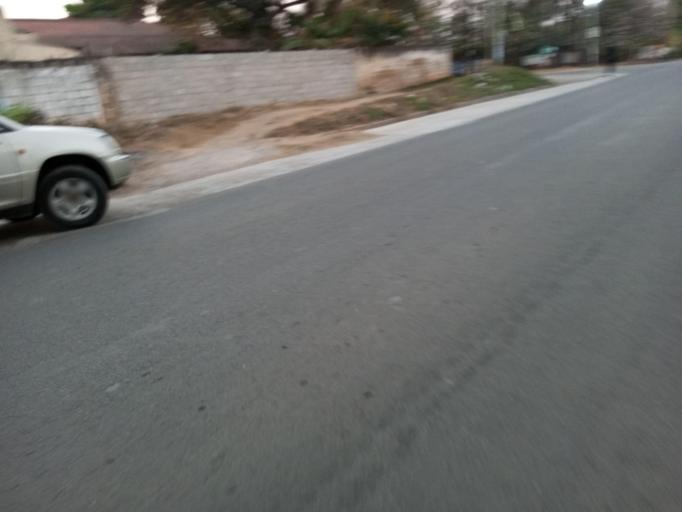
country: ZM
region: Lusaka
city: Lusaka
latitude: -15.4018
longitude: 28.2967
